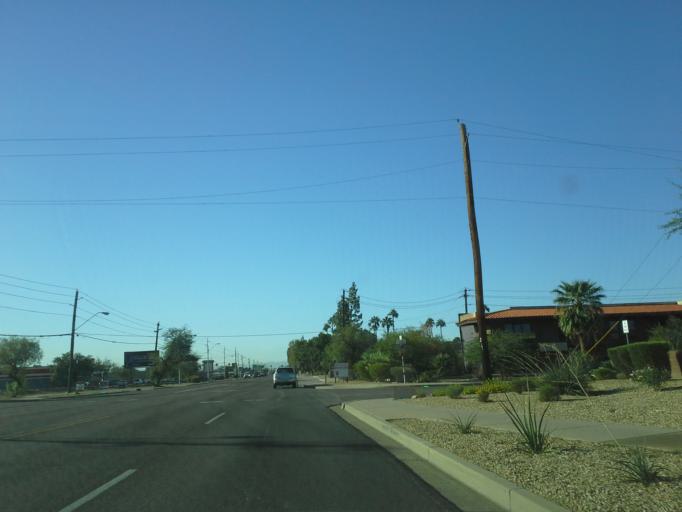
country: US
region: Arizona
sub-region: Maricopa County
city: Glendale
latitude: 33.5898
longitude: -112.0998
